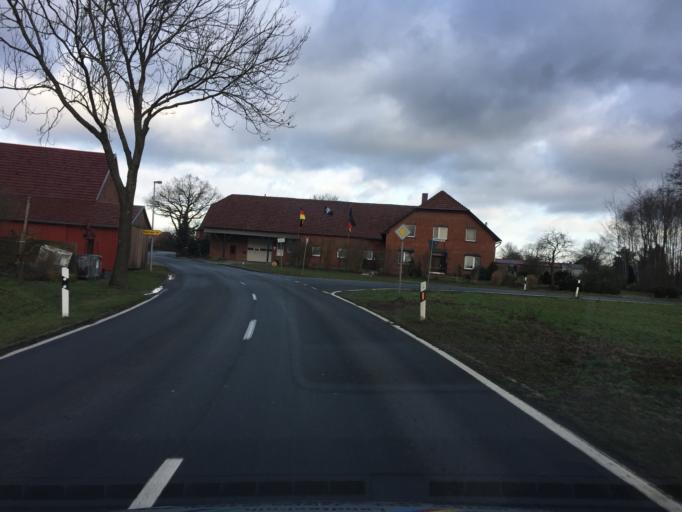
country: DE
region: Lower Saxony
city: Raddestorf
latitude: 52.4992
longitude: 8.9934
